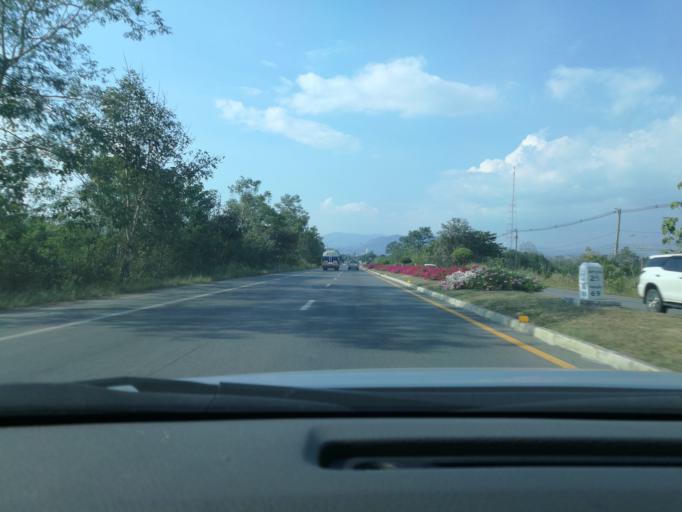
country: TH
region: Phetchabun
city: Phetchabun
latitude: 16.2437
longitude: 101.0744
